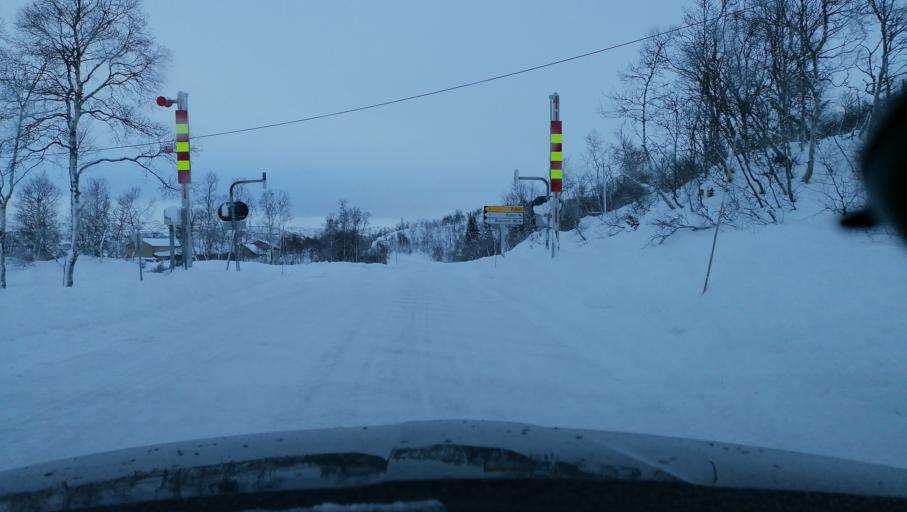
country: NO
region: Aust-Agder
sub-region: Bykle
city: Hovden
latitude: 59.6403
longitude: 7.4549
